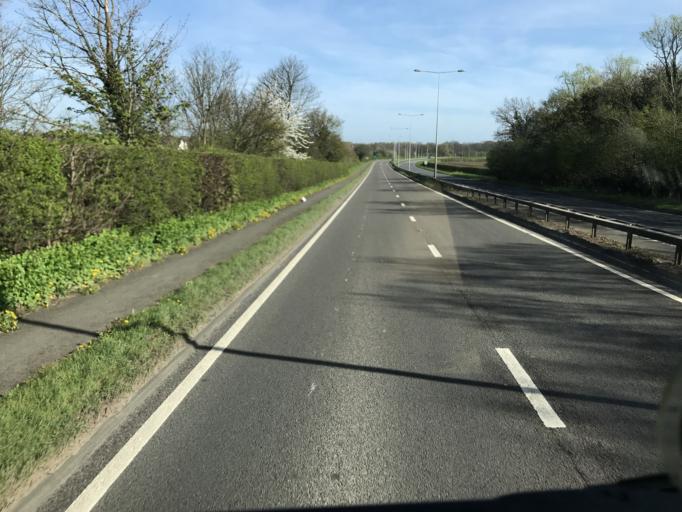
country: GB
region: England
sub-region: Cheshire West and Chester
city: Marston
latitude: 53.2693
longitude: -2.4551
